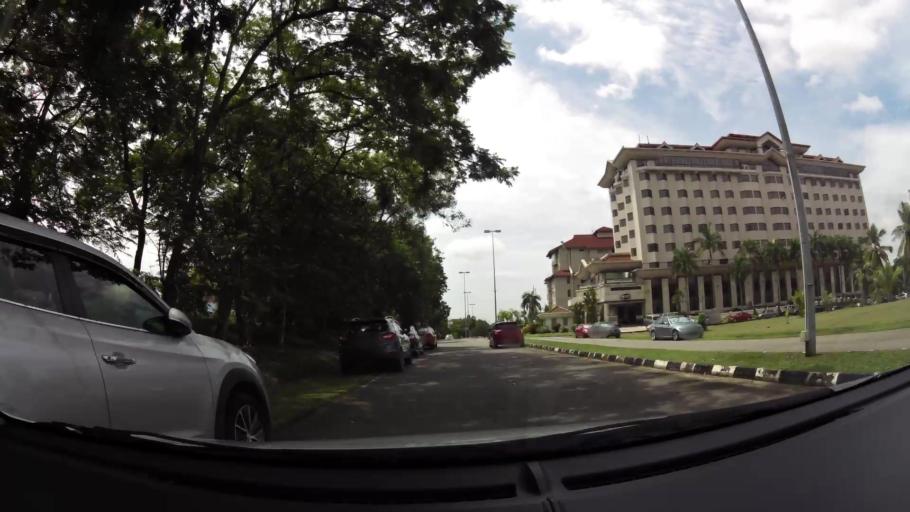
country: BN
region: Brunei and Muara
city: Bandar Seri Begawan
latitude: 4.9319
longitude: 114.9444
